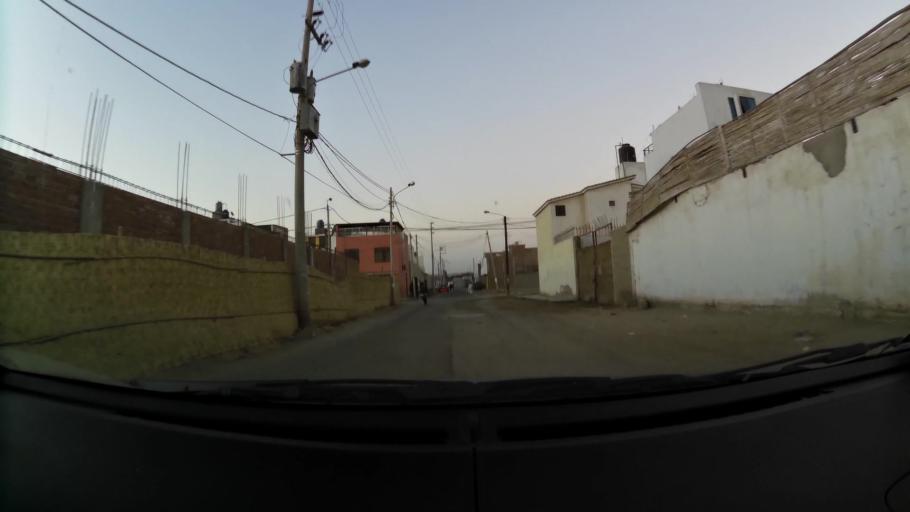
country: PE
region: Ancash
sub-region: Provincia de Santa
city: Buenos Aires
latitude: -9.1224
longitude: -78.5357
